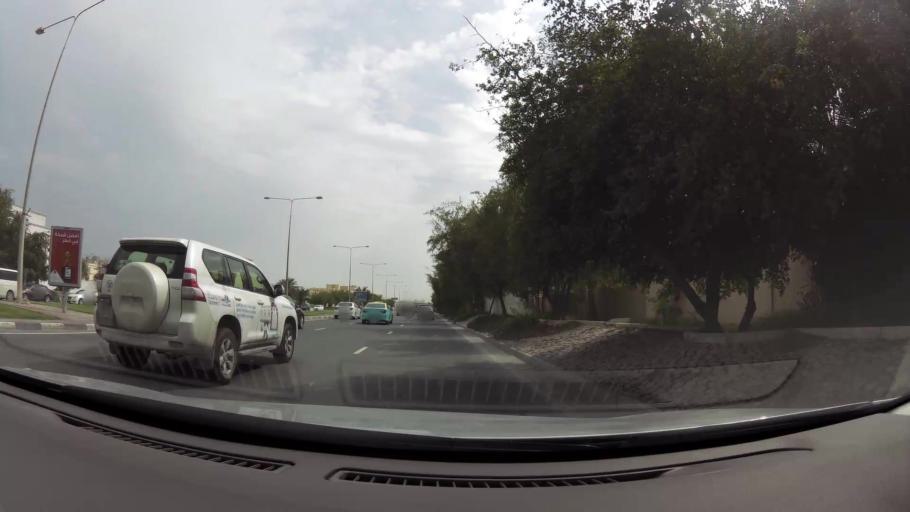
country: QA
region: Baladiyat ad Dawhah
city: Doha
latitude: 25.3410
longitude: 51.5058
